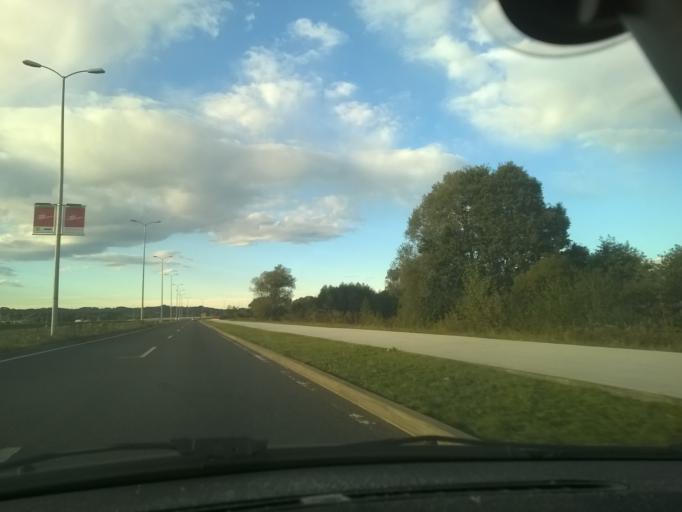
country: HR
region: Zagrebacka
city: Zapresic
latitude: 45.8743
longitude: 15.8202
